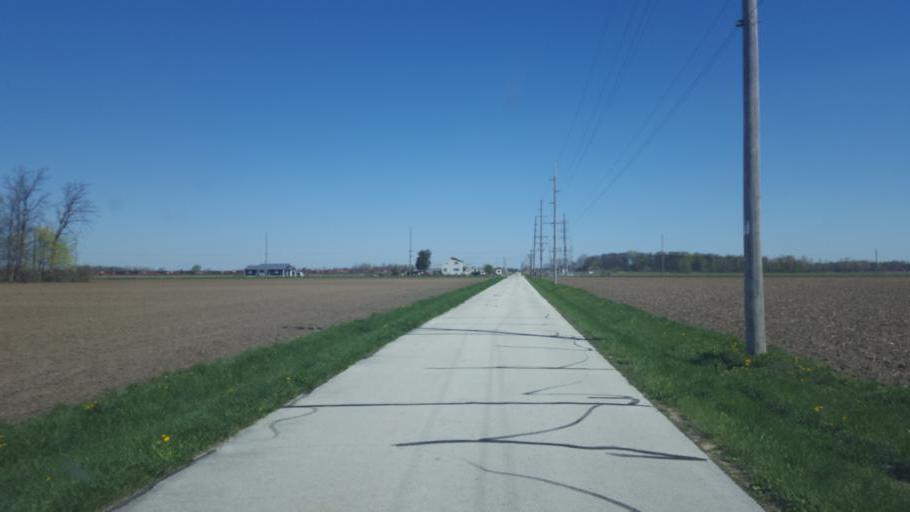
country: US
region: Ohio
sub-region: Seneca County
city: Tiffin
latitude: 41.2236
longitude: -83.1869
